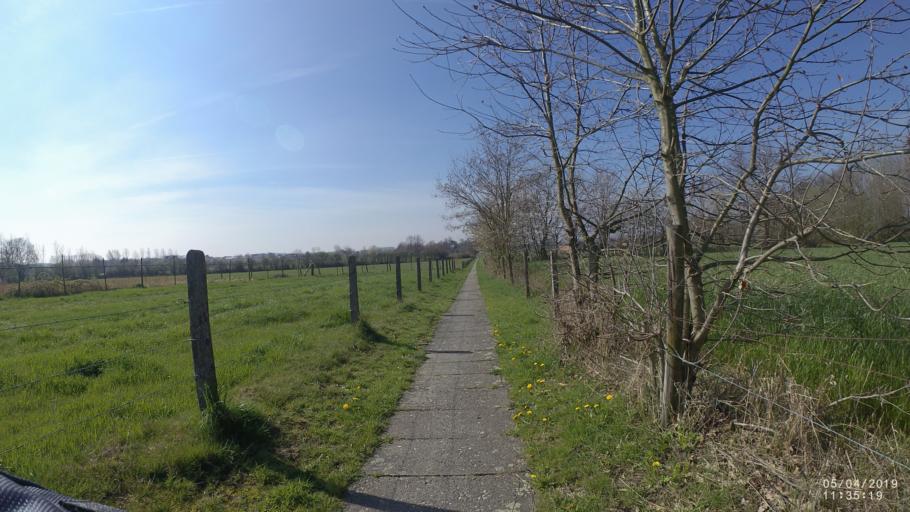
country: BE
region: Flanders
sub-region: Provincie Limburg
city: Herk-de-Stad
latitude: 50.9001
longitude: 5.1715
